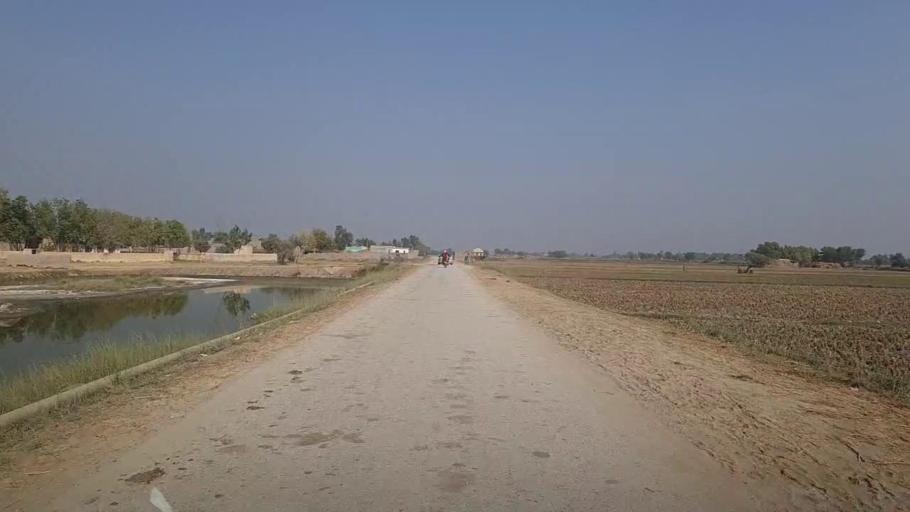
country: PK
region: Sindh
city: Kandhkot
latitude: 28.2310
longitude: 69.2140
